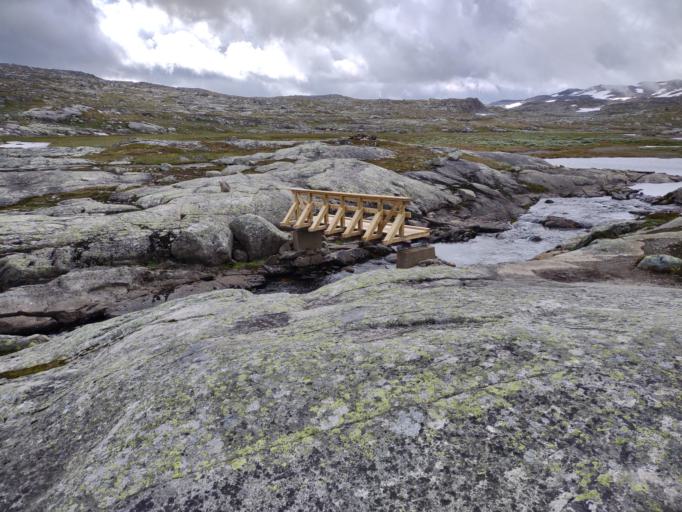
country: NO
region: Hordaland
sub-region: Eidfjord
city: Eidfjord
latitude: 60.5610
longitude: 7.5338
